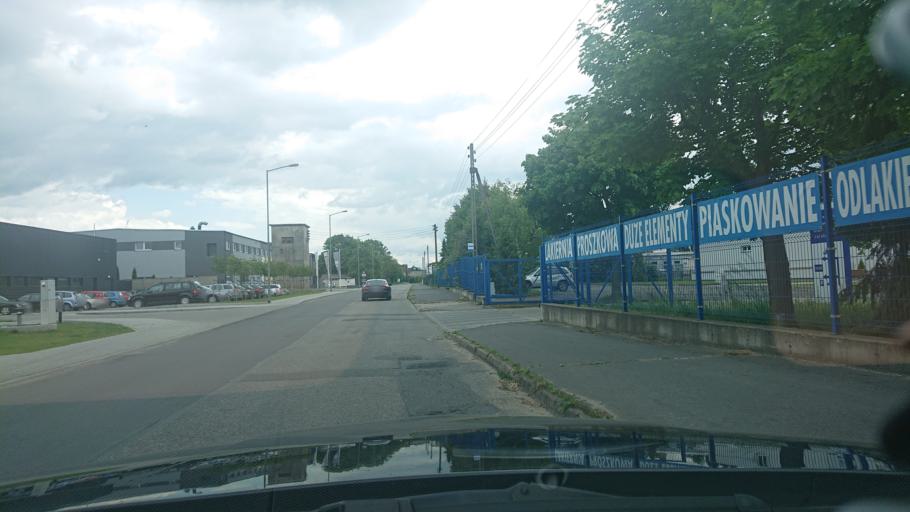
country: PL
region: Greater Poland Voivodeship
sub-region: Powiat gnieznienski
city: Gniezno
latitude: 52.5379
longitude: 17.6292
